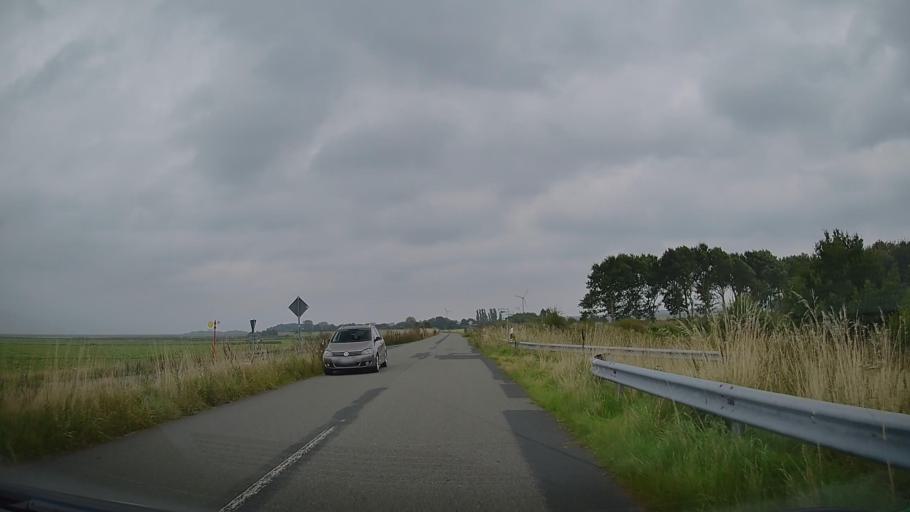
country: DE
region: Lower Saxony
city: Neuhaus an der Oste
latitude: 53.8206
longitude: 9.0438
